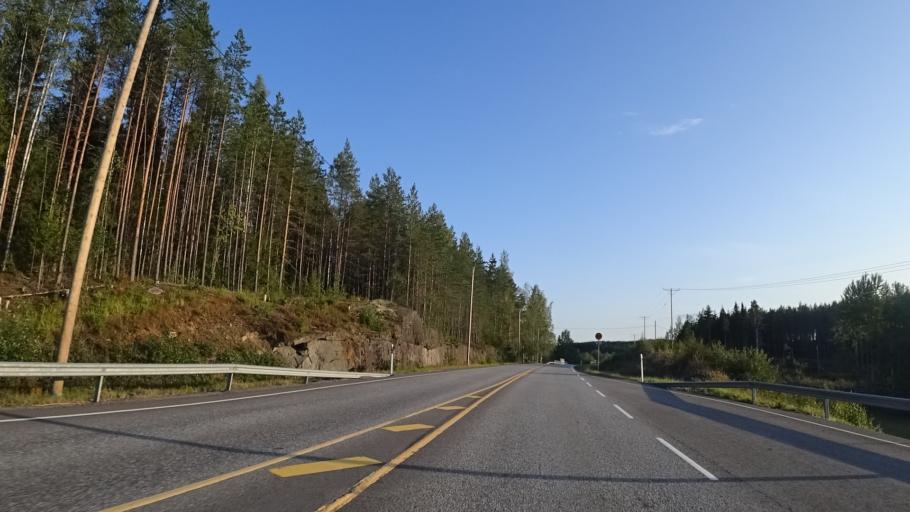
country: FI
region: South Karelia
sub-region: Lappeenranta
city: Lappeenranta
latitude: 60.9110
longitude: 28.1340
